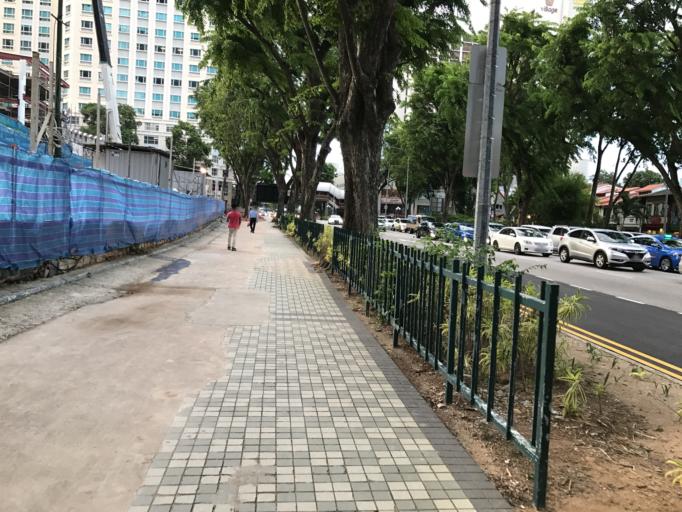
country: SG
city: Singapore
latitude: 1.3005
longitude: 103.8585
